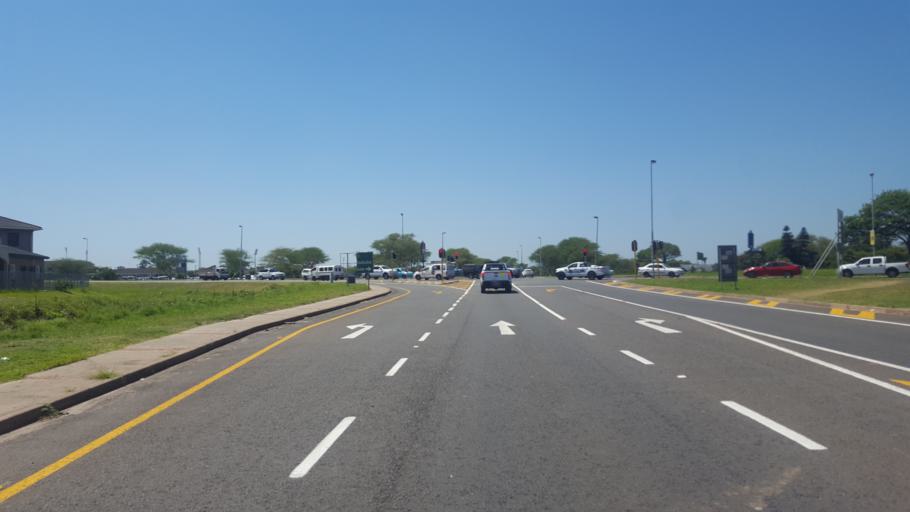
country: ZA
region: KwaZulu-Natal
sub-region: uThungulu District Municipality
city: Richards Bay
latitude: -28.7513
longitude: 32.0551
